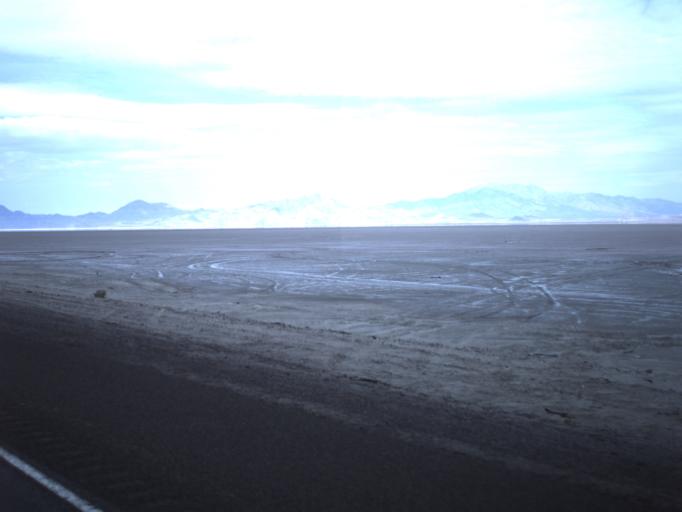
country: US
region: Utah
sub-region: Tooele County
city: Wendover
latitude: 40.7372
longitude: -113.7417
